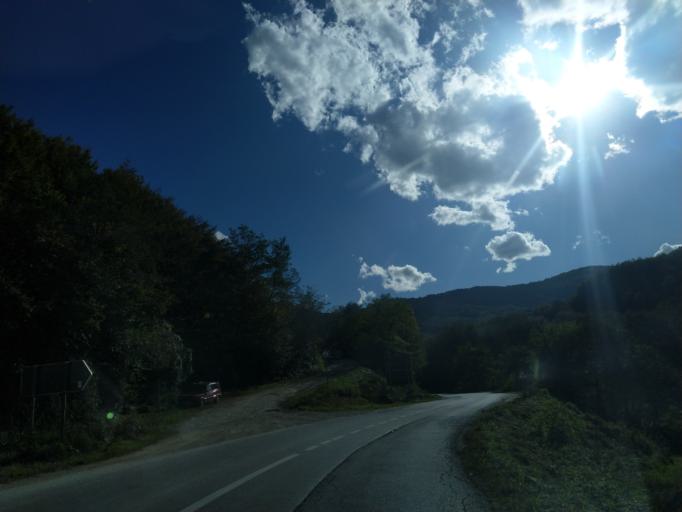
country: RS
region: Central Serbia
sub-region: Zlatiborski Okrug
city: Uzice
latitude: 43.8857
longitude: 19.7783
